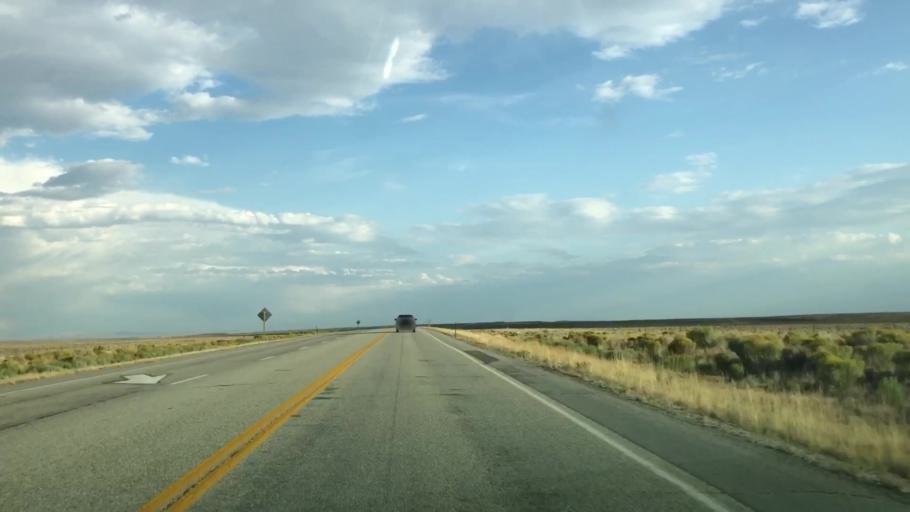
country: US
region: Wyoming
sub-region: Sublette County
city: Marbleton
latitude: 42.3196
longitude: -109.5080
